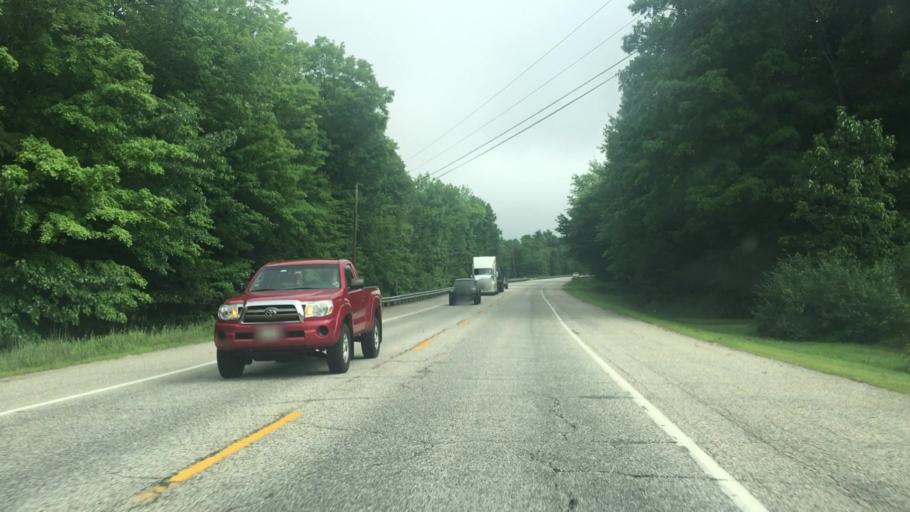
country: US
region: Maine
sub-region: Oxford County
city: Paris
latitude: 44.2600
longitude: -70.5145
